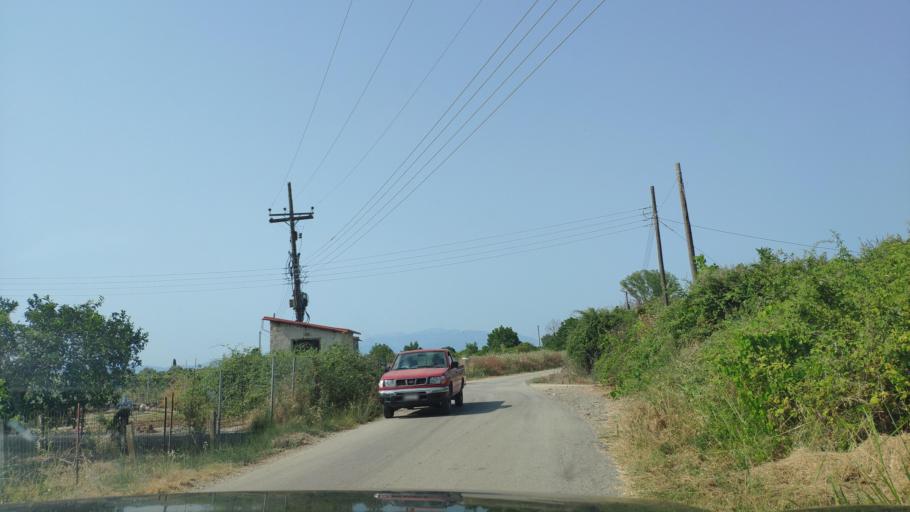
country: GR
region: Epirus
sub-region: Nomos Artas
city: Kompoti
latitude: 39.0734
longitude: 21.0825
